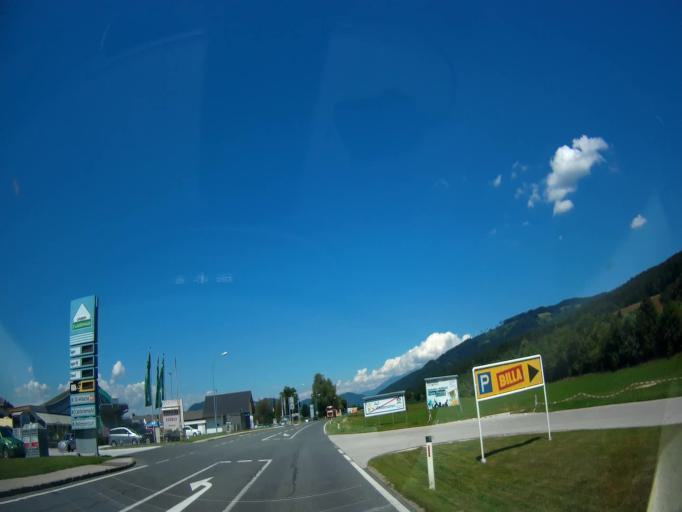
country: AT
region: Carinthia
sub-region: Politischer Bezirk Volkermarkt
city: Bleiburg/Pliberk
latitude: 46.5928
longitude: 14.7953
